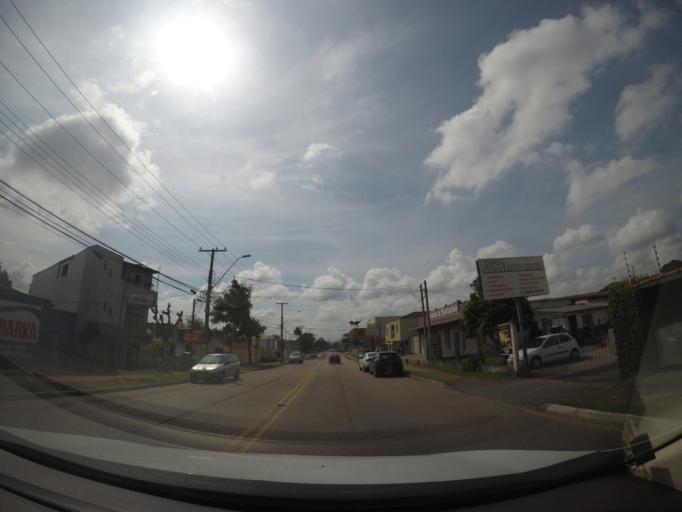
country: BR
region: Parana
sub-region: Curitiba
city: Curitiba
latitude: -25.4817
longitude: -49.2694
